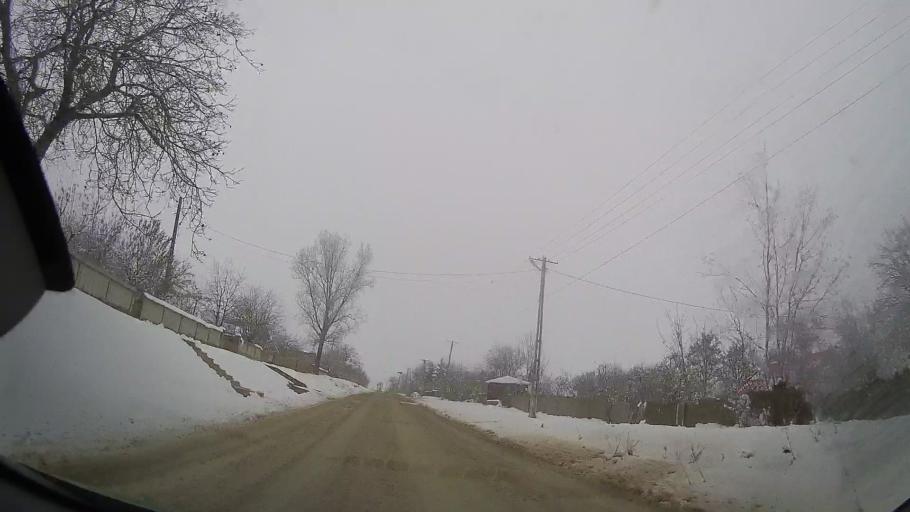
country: RO
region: Vaslui
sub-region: Comuna Todiresti
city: Todiresti
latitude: 46.8761
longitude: 27.3763
